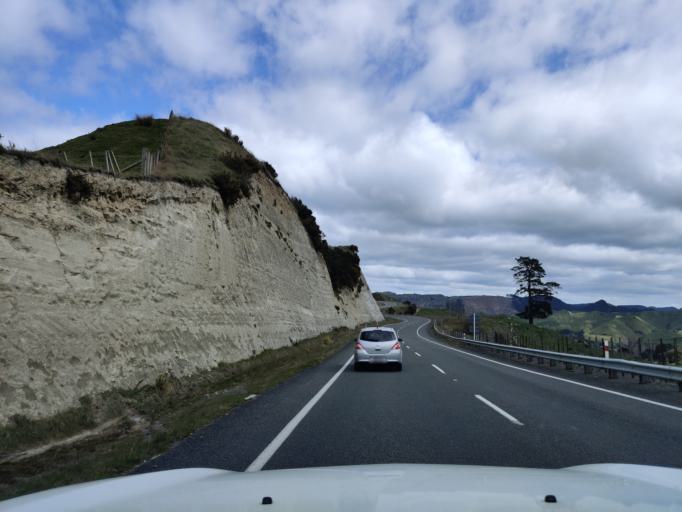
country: NZ
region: Manawatu-Wanganui
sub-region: Wanganui District
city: Wanganui
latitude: -39.7839
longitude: 175.2236
